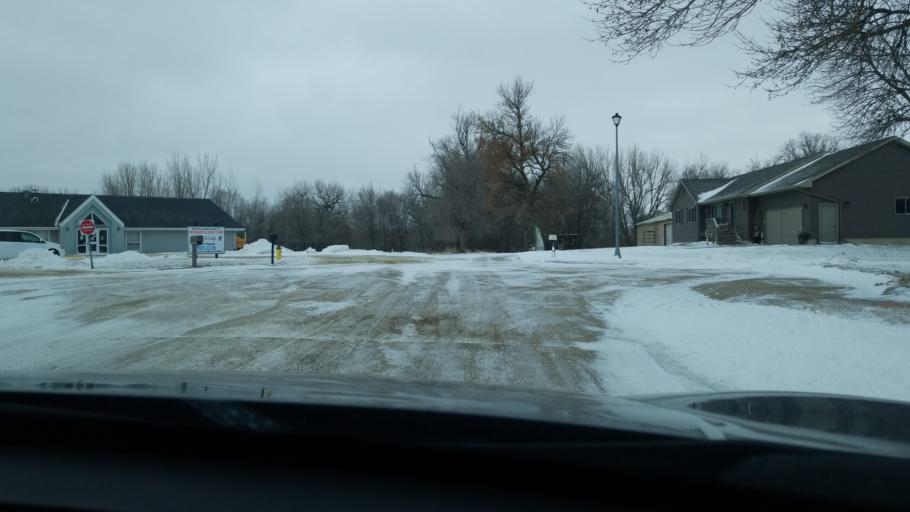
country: US
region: Iowa
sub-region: Lyon County
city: Rock Rapids
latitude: 43.4309
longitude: -96.1582
